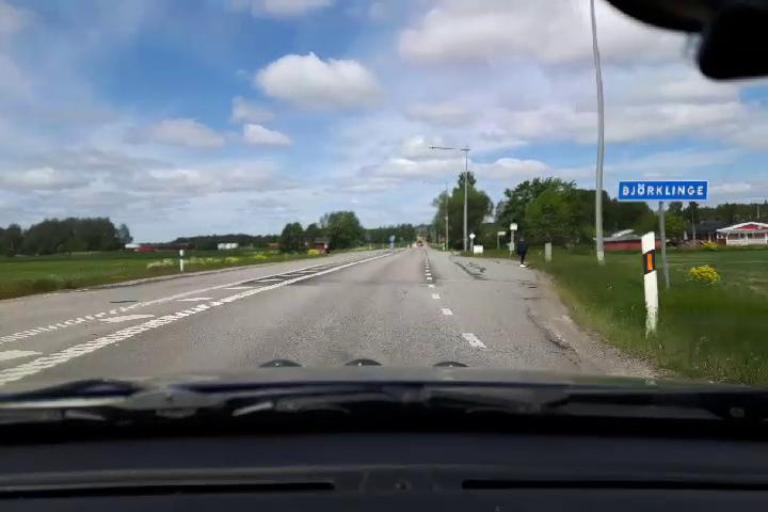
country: SE
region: Uppsala
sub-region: Osthammars Kommun
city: Bjorklinge
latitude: 60.0186
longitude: 17.5563
